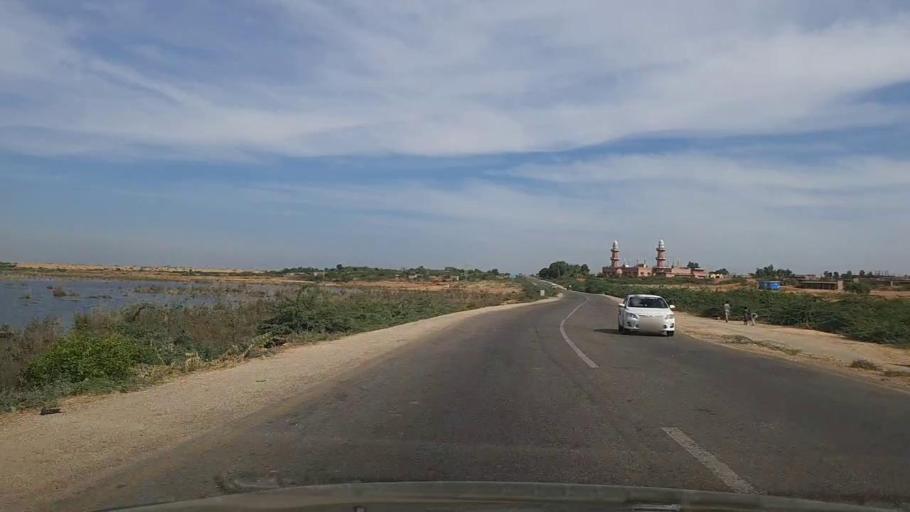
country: PK
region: Sindh
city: Thatta
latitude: 24.8287
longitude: 67.9934
